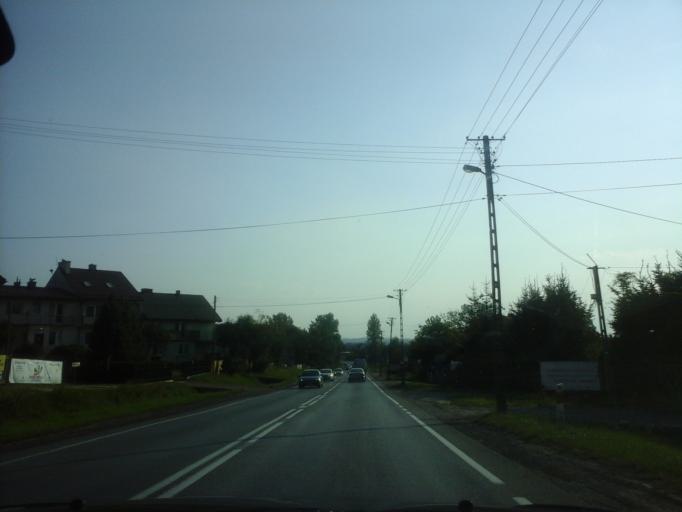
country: PL
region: Lesser Poland Voivodeship
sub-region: Powiat krakowski
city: Skawina
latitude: 49.9870
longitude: 19.8423
